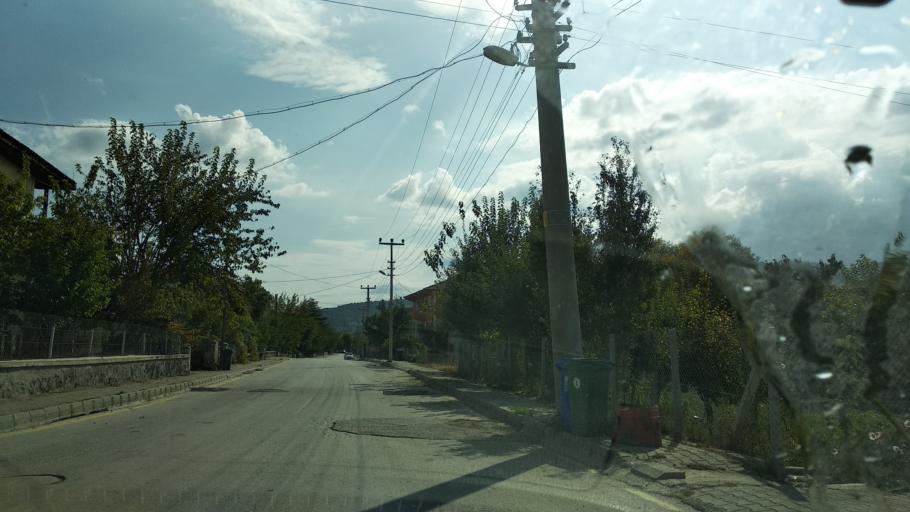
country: TR
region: Bolu
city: Seben
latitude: 40.4122
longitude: 31.5685
